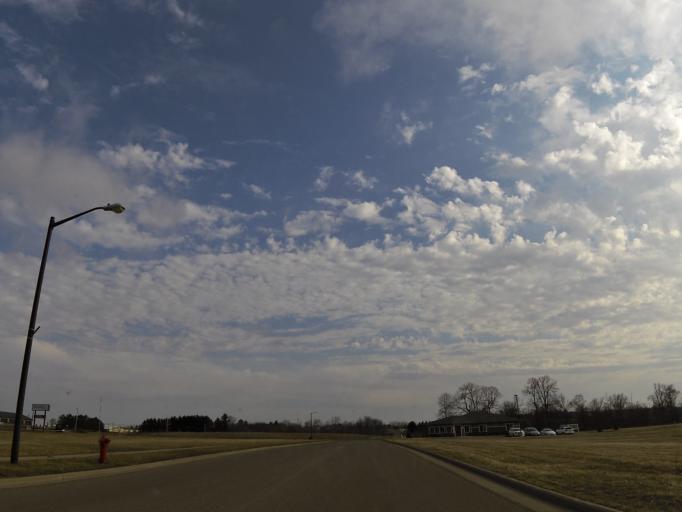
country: US
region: Wisconsin
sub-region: Pierce County
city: Ellsworth
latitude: 44.7479
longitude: -92.4885
